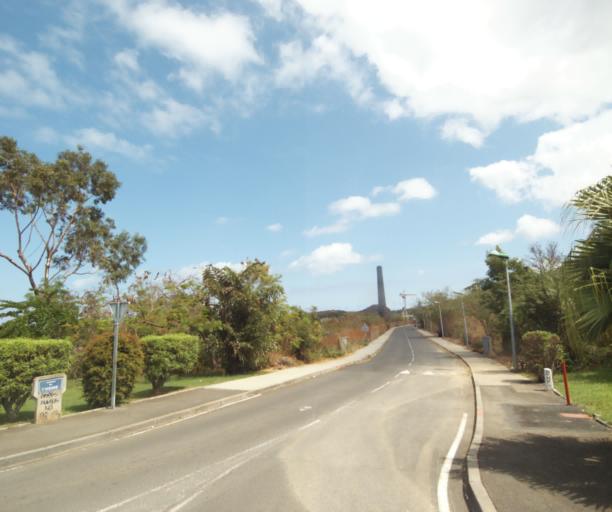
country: RE
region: Reunion
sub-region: Reunion
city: Trois-Bassins
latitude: -21.0842
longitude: 55.2376
